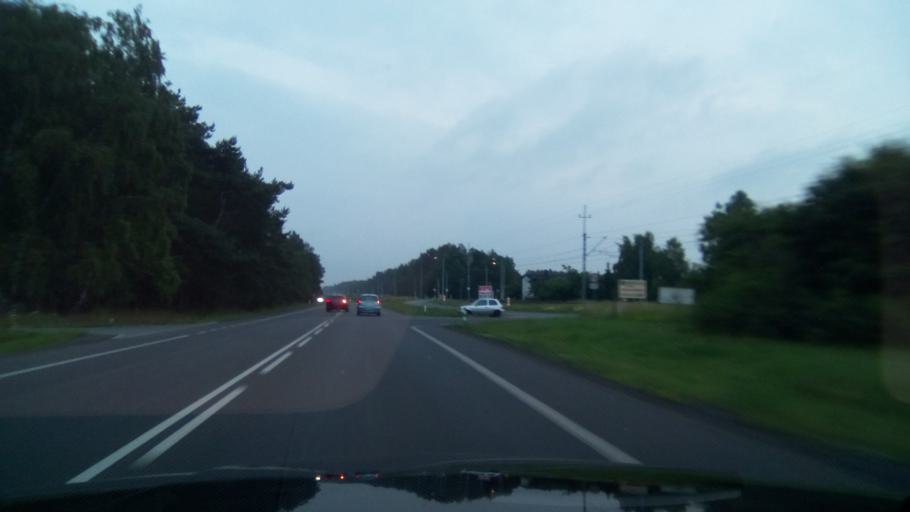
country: PL
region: Greater Poland Voivodeship
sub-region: Powiat poznanski
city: Kostrzyn
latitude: 52.4691
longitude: 17.1868
